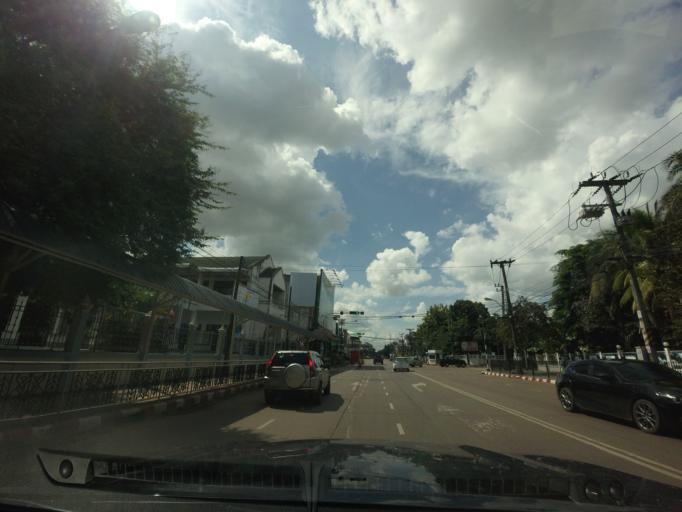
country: TH
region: Changwat Udon Thani
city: Udon Thani
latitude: 17.4094
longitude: 102.7786
